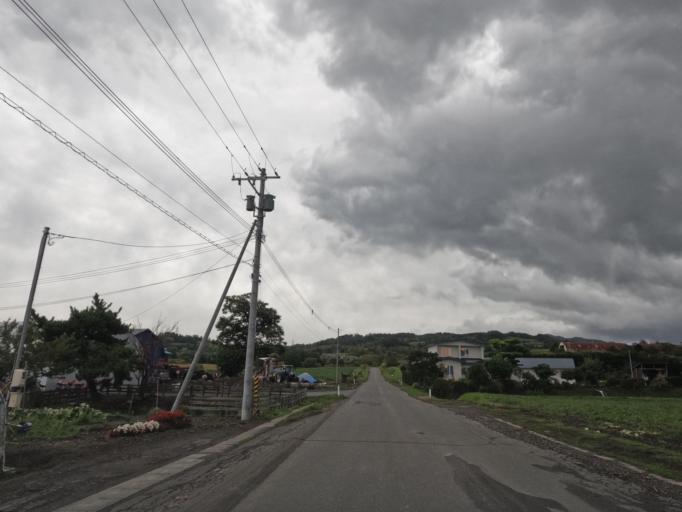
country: JP
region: Hokkaido
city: Date
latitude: 42.5038
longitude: 140.8887
